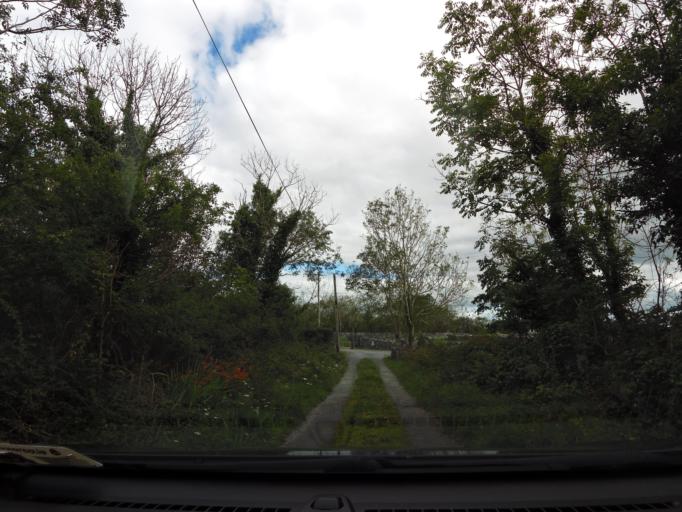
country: IE
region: Connaught
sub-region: County Galway
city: Moycullen
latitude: 53.3246
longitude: -9.1209
